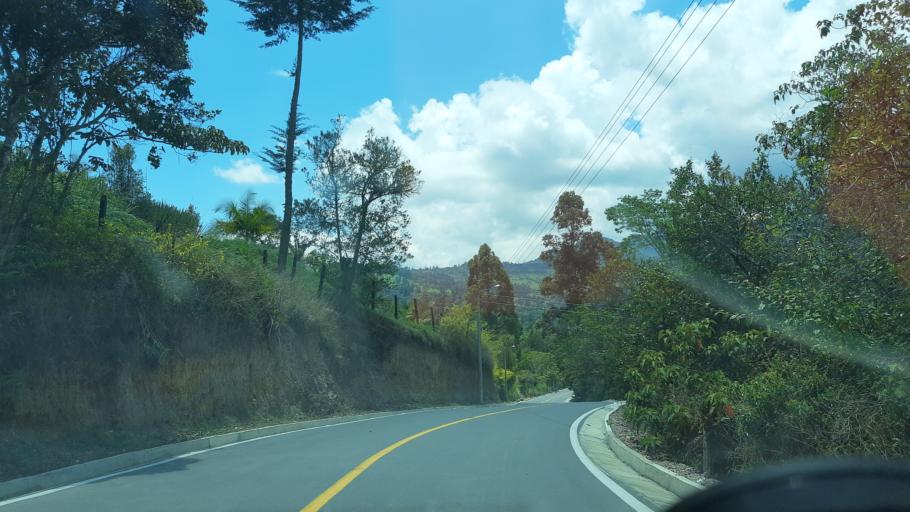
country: CO
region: Boyaca
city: Chinavita
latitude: 5.1344
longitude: -73.3882
